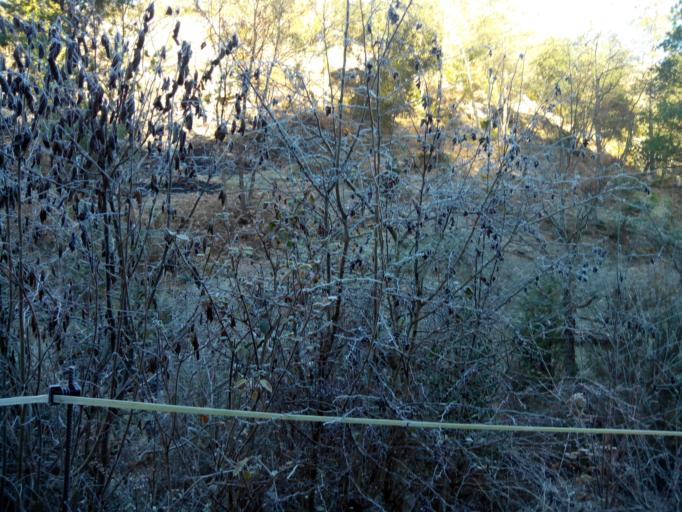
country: ES
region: Catalonia
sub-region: Provincia de Barcelona
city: Vilada
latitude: 42.1050
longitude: 1.9461
